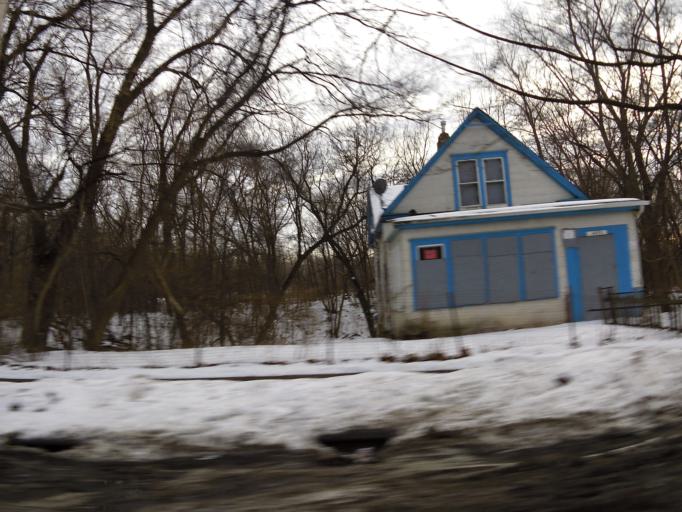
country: US
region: Minnesota
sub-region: Ramsey County
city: Maplewood
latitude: 44.9667
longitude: -93.0376
